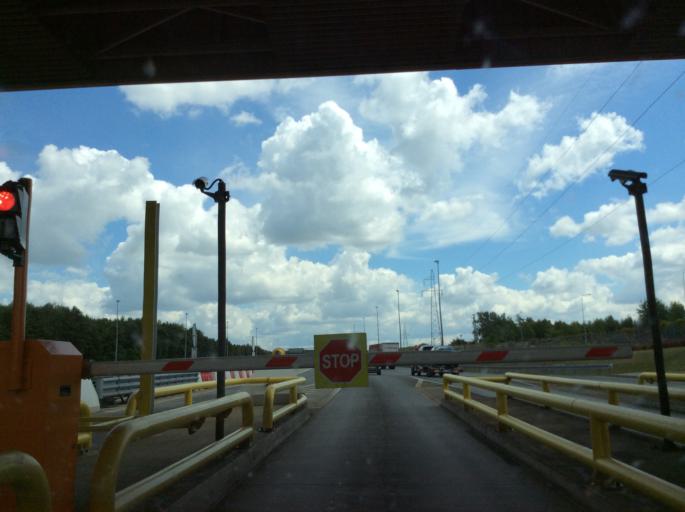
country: PL
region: Greater Poland Voivodeship
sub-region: Powiat koninski
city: Stare Miasto
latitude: 52.1523
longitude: 18.2776
